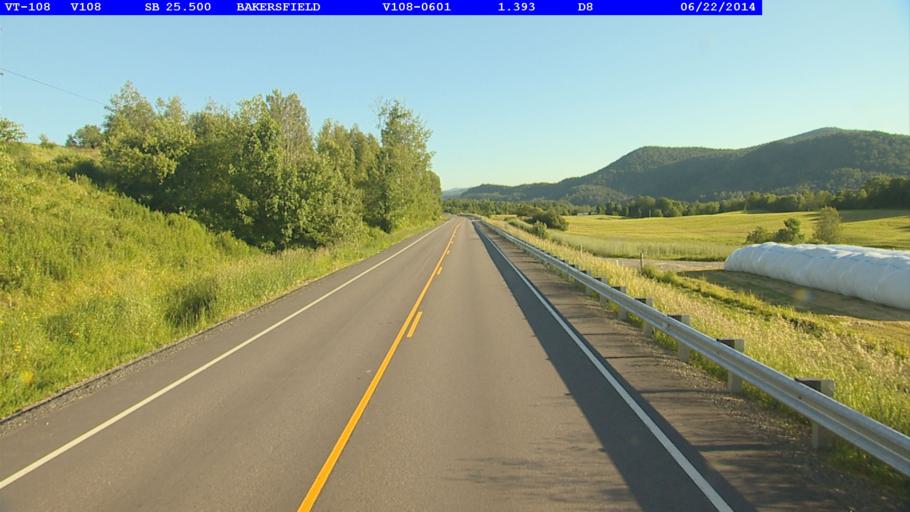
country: US
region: Vermont
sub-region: Franklin County
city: Enosburg Falls
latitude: 44.7531
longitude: -72.8225
